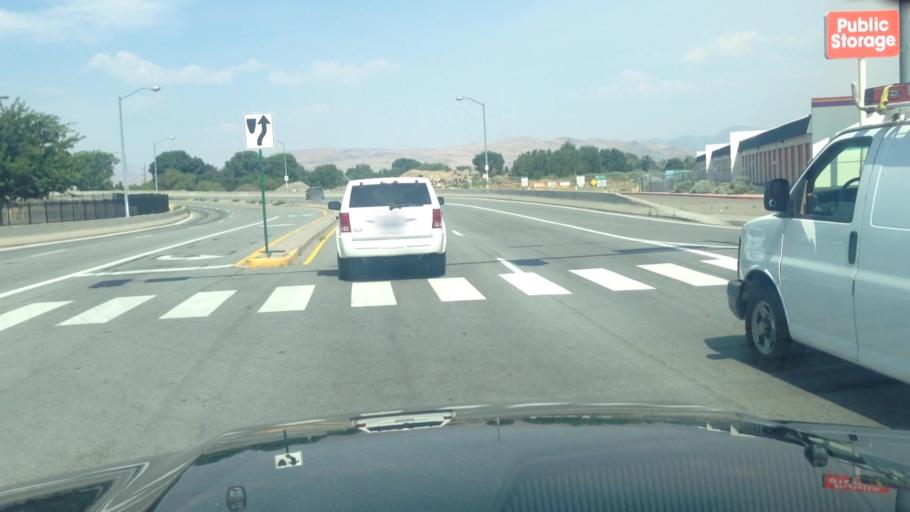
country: US
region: Nevada
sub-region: Washoe County
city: Sparks
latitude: 39.5201
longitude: -119.7739
